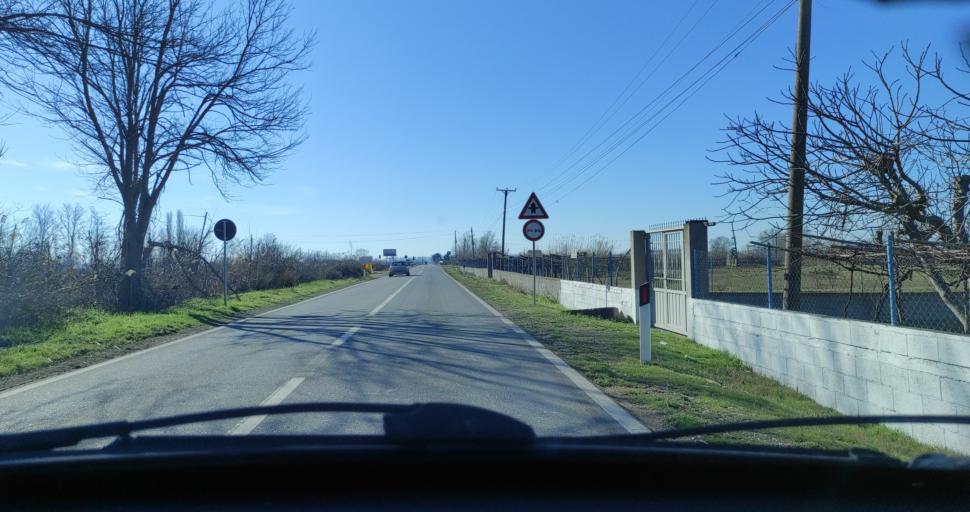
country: AL
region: Shkoder
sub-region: Rrethi i Shkodres
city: Velipoje
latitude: 41.8950
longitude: 19.4031
